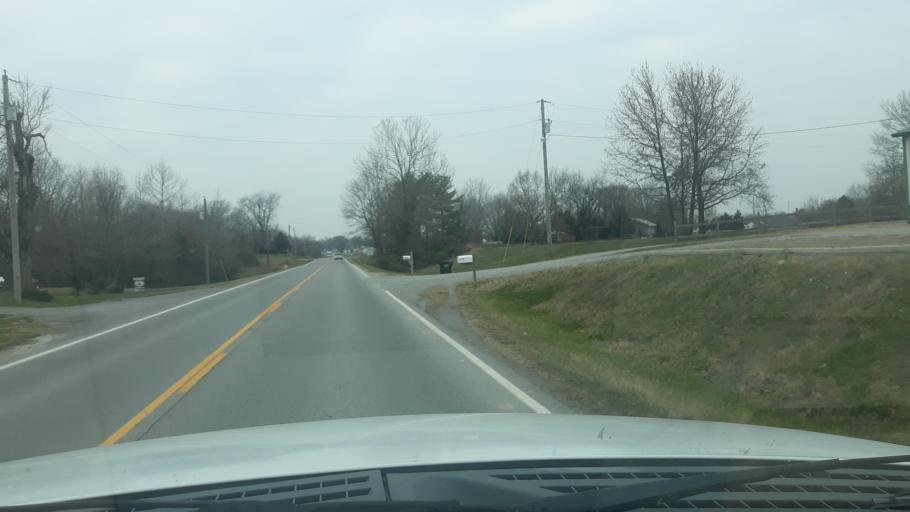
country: US
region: Illinois
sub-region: Saline County
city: Harrisburg
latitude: 37.8369
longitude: -88.5939
